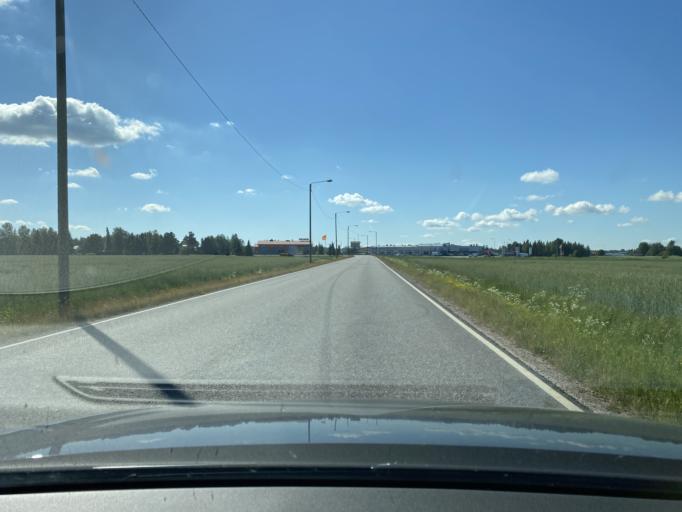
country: FI
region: Satakunta
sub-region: Pori
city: Huittinen
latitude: 61.1651
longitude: 22.6984
